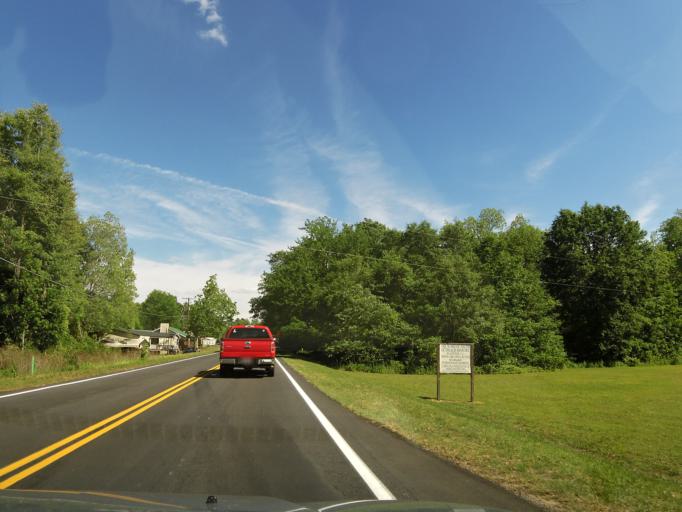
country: US
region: South Carolina
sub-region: Barnwell County
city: Blackville
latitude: 33.3501
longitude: -81.2603
